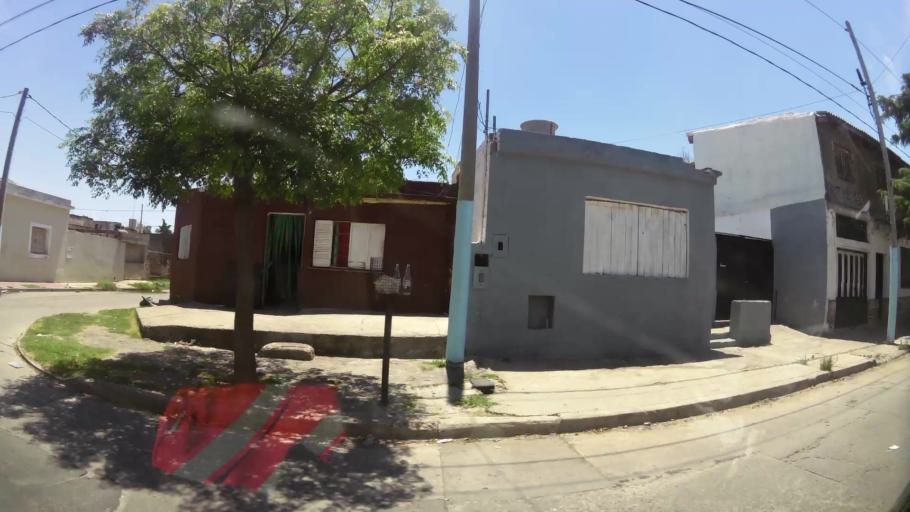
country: AR
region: Cordoba
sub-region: Departamento de Capital
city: Cordoba
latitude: -31.3970
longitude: -64.2057
